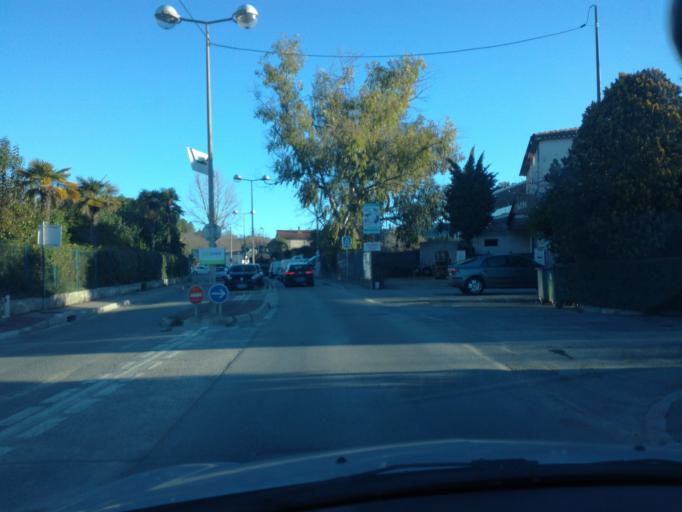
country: FR
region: Provence-Alpes-Cote d'Azur
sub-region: Departement des Alpes-Maritimes
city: La Roquette-sur-Siagne
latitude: 43.6056
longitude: 6.9717
